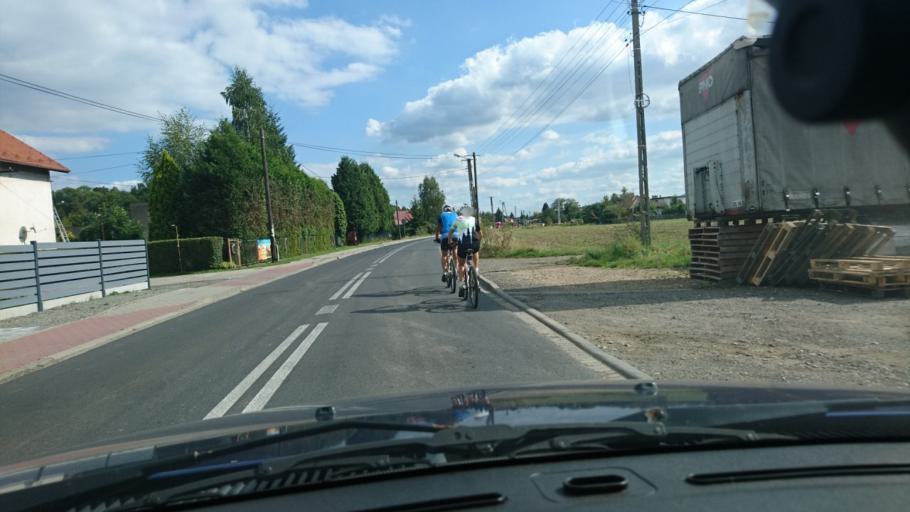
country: PL
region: Silesian Voivodeship
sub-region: Powiat bielski
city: Mazancowice
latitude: 49.8665
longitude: 18.9689
